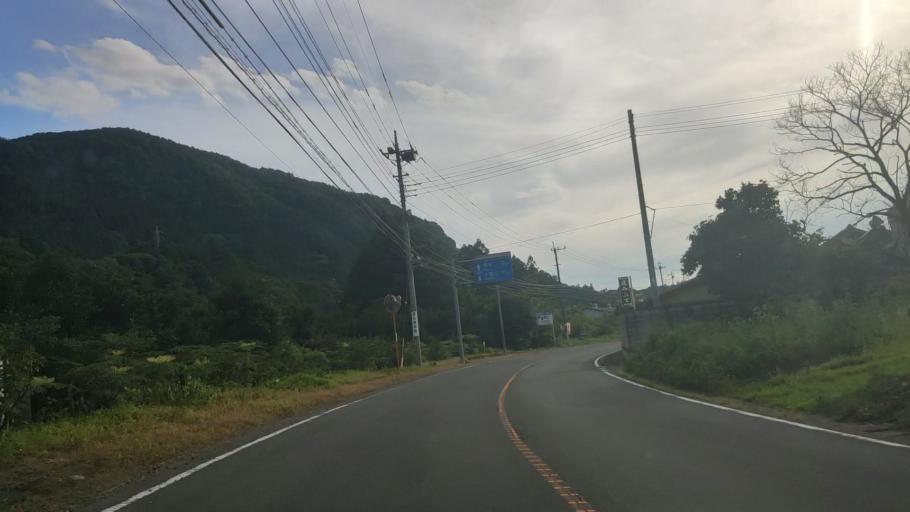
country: JP
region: Gunma
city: Omamacho-omama
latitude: 36.5015
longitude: 139.2908
